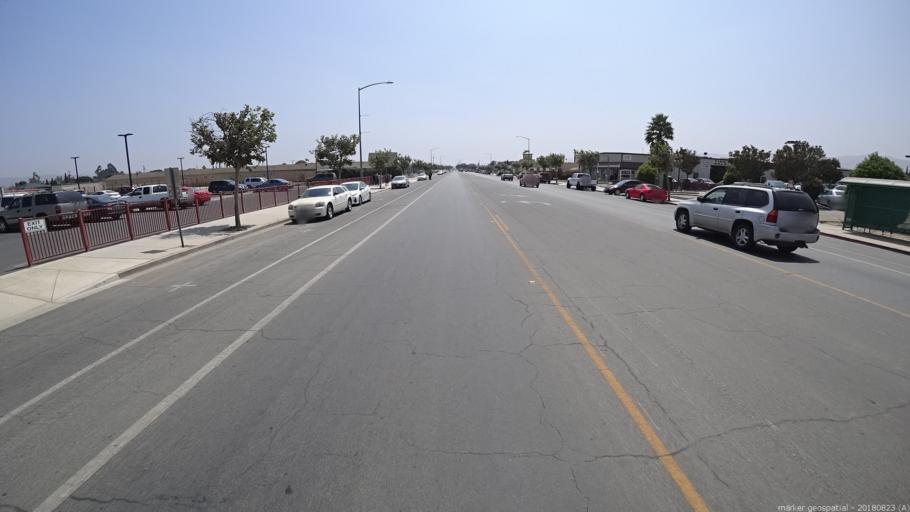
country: US
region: California
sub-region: Monterey County
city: Greenfield
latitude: 36.3260
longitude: -121.2477
